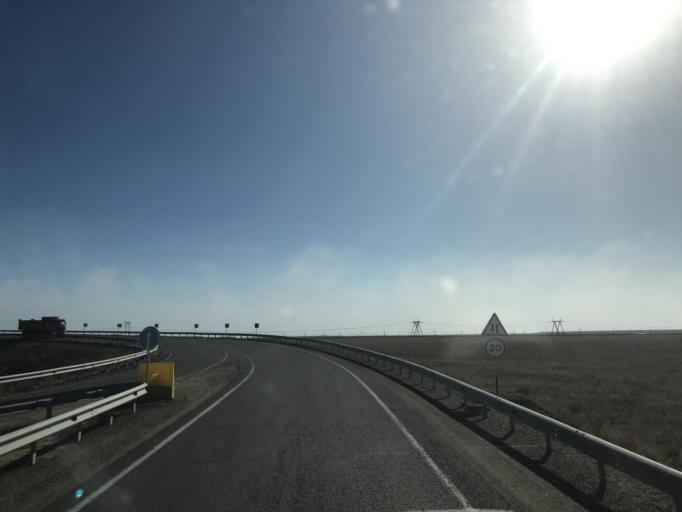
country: KZ
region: Pavlodar
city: Leninskiy
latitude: 52.1538
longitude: 76.8188
